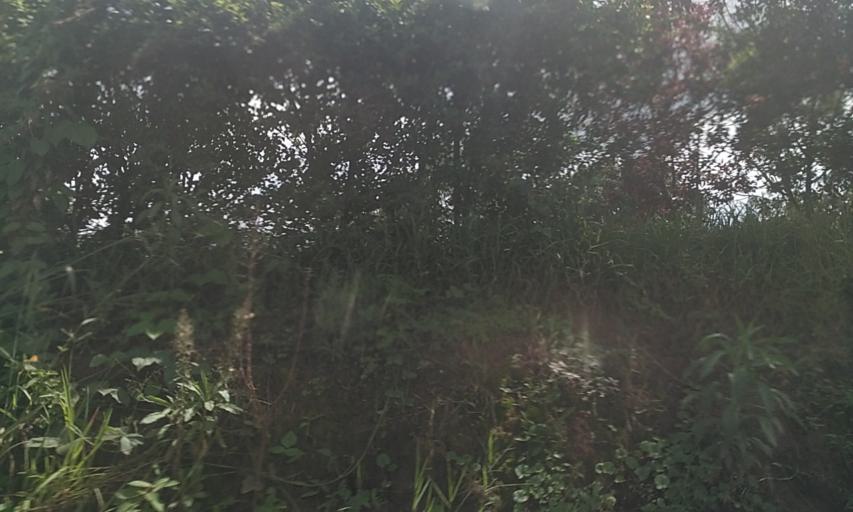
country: UG
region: Central Region
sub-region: Wakiso District
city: Wakiso
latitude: 0.3940
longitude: 32.4593
